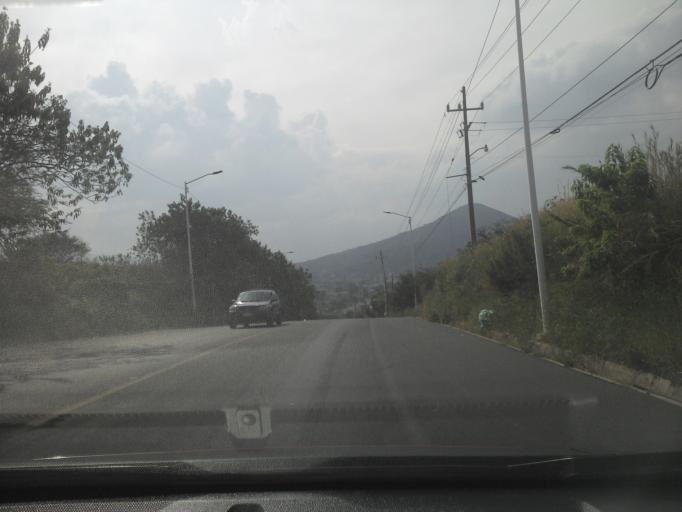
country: MX
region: Jalisco
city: Tlajomulco de Zuniga
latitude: 20.4801
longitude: -103.4330
